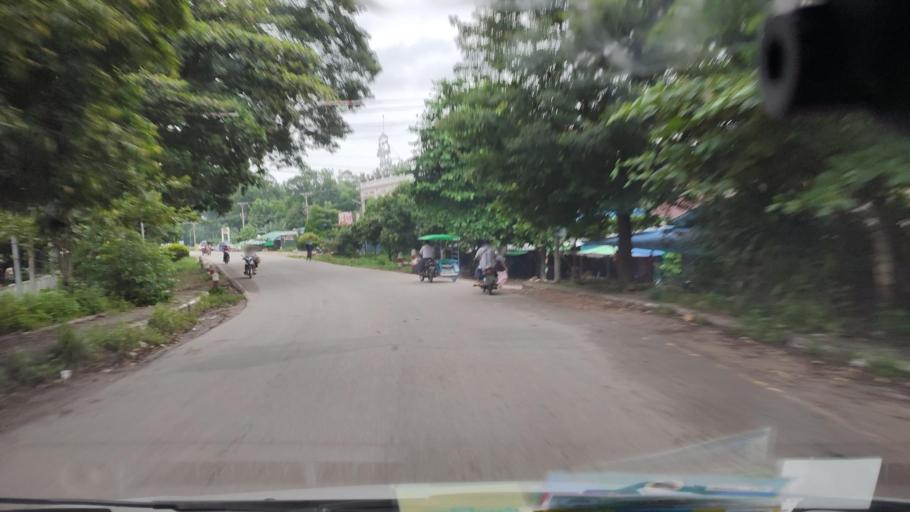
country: MM
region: Bago
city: Taungoo
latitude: 18.9427
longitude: 96.4481
